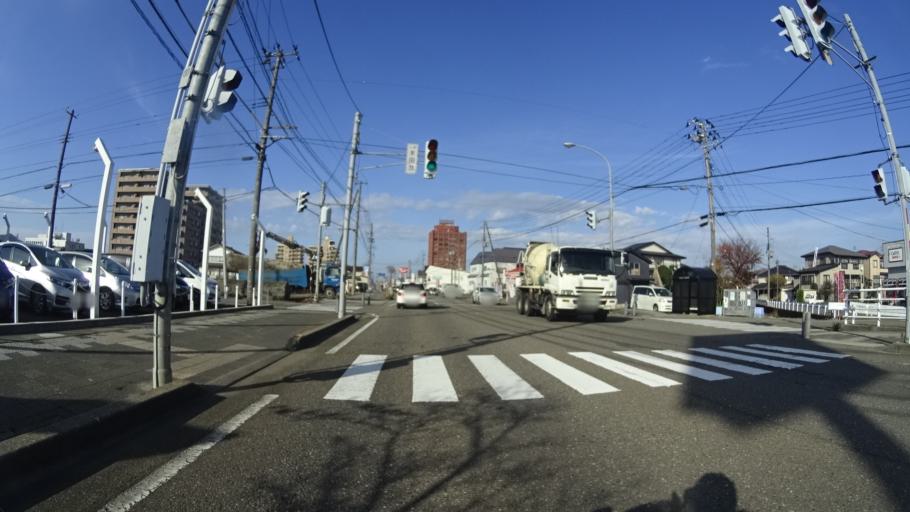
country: JP
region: Niigata
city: Joetsu
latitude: 37.1455
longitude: 138.2398
